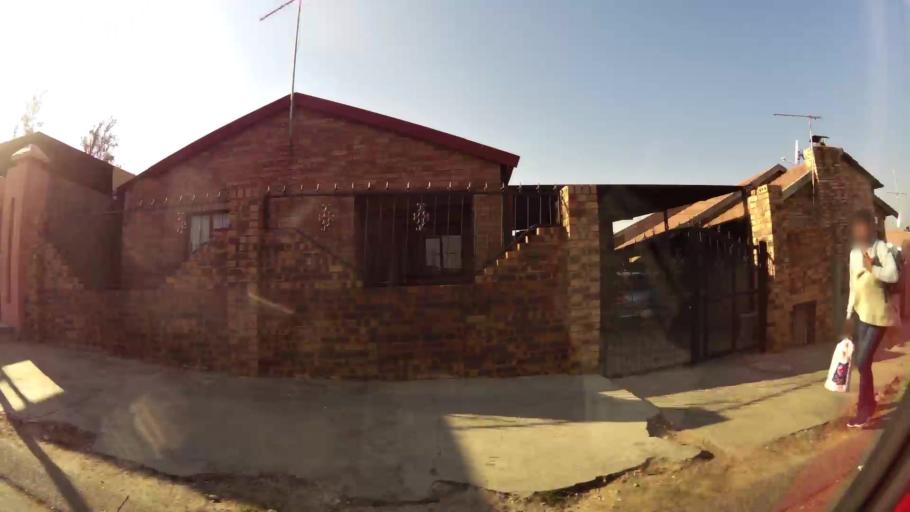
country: ZA
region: Gauteng
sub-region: City of Johannesburg Metropolitan Municipality
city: Soweto
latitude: -26.2538
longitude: 27.9493
